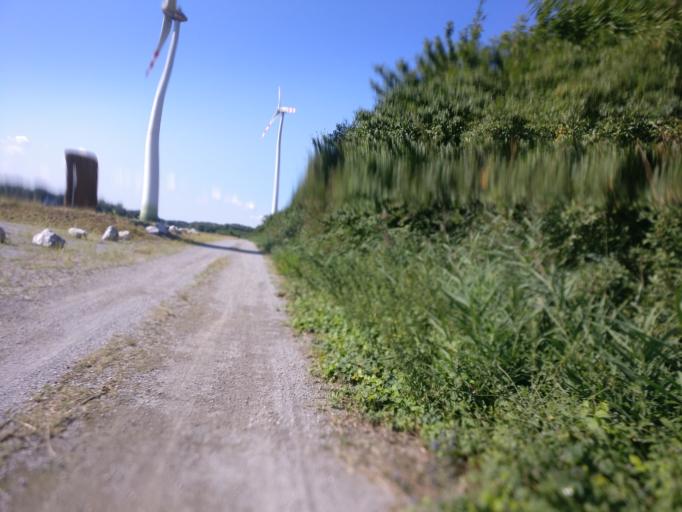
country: AT
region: Lower Austria
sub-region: Politischer Bezirk Baden
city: Ebreichsdorf
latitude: 47.9372
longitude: 16.3753
